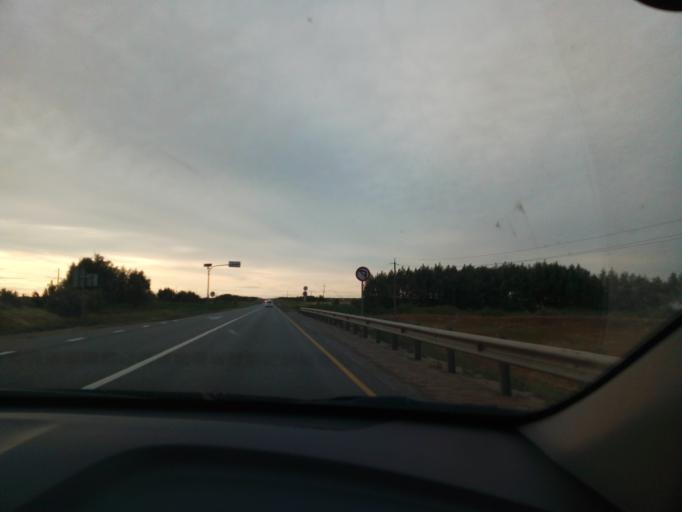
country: RU
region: Volgograd
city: Primorsk
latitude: 49.2673
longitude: 44.8789
